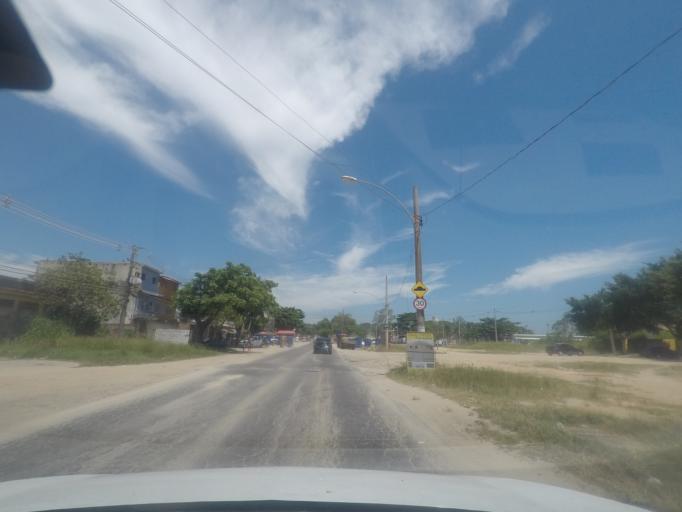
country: BR
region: Rio de Janeiro
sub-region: Itaguai
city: Itaguai
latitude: -22.9833
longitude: -43.6612
